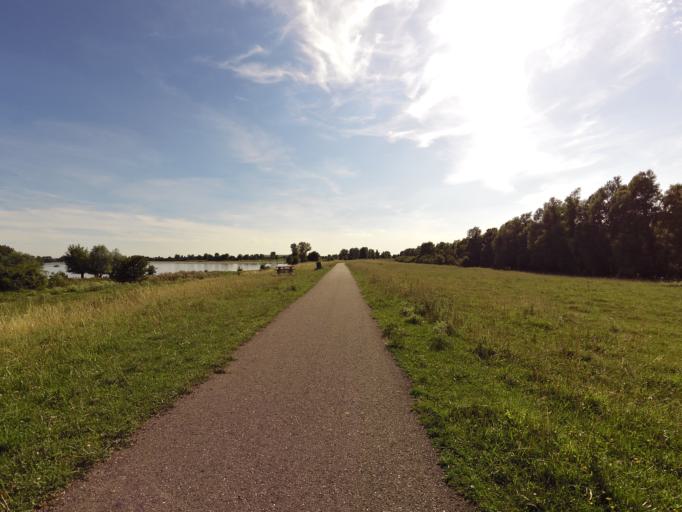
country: NL
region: Gelderland
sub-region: Gemeente Zevenaar
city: Zevenaar
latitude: 51.8735
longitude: 6.0856
